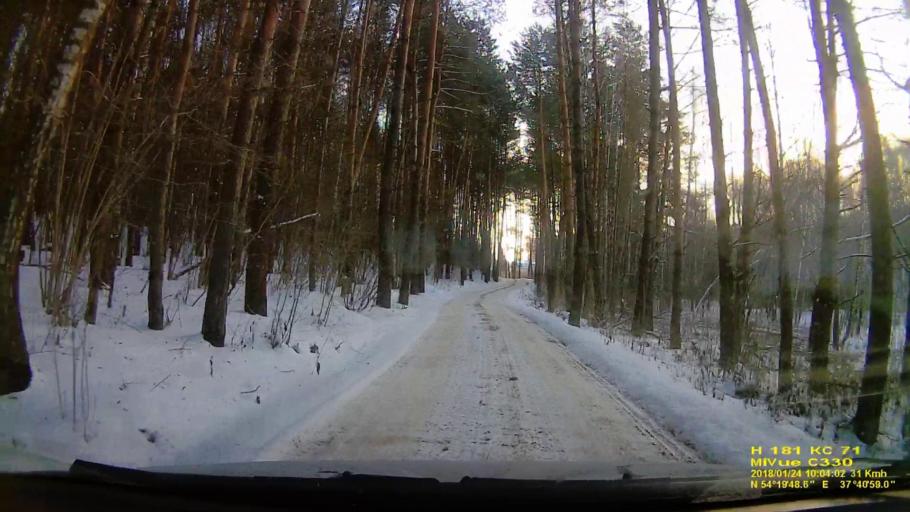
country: RU
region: Tula
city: Revyakino
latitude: 54.3302
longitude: 37.6831
